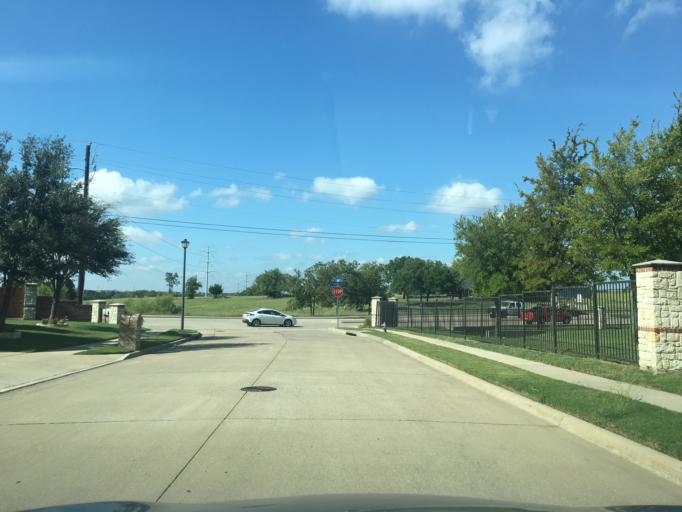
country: US
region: Texas
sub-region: Dallas County
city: Sachse
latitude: 32.9638
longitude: -96.5998
